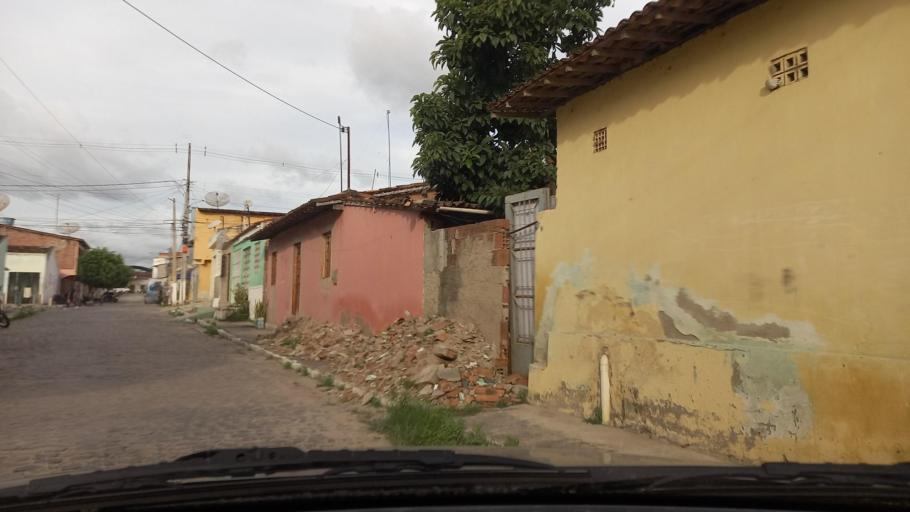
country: BR
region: Pernambuco
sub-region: Gravata
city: Gravata
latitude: -8.2048
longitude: -35.5648
